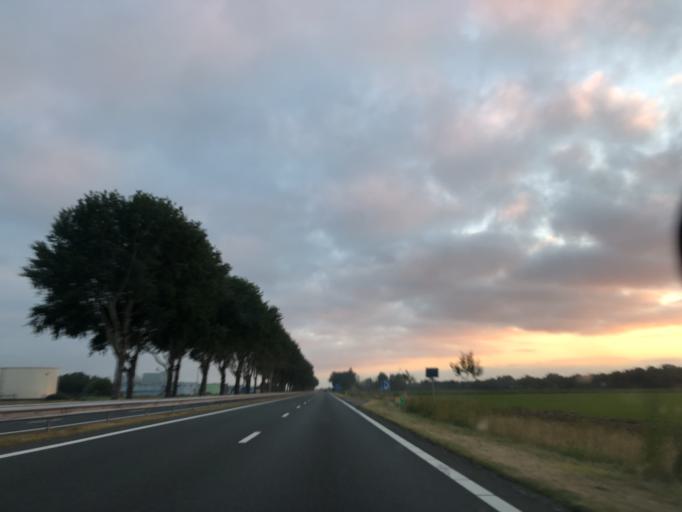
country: NL
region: Groningen
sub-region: Gemeente Veendam
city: Veendam
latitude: 53.1157
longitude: 6.8994
